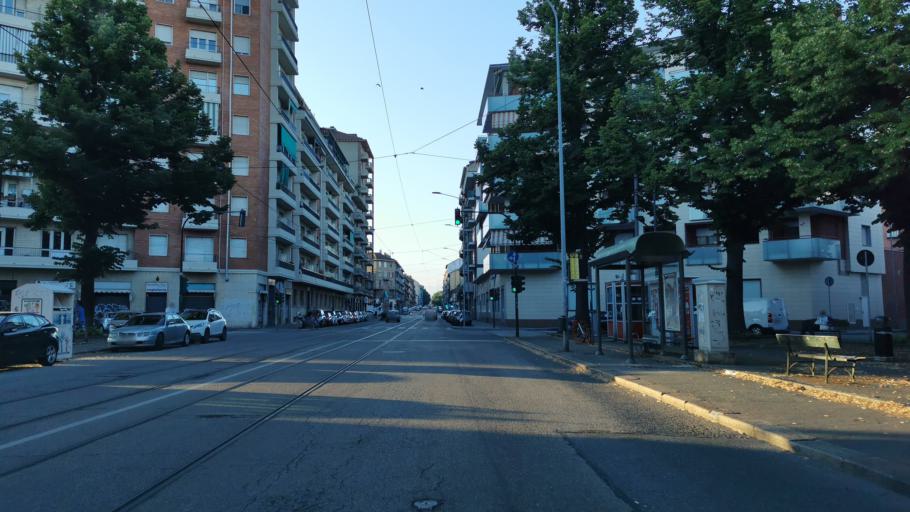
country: IT
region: Piedmont
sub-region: Provincia di Torino
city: Turin
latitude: 45.0847
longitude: 7.6931
